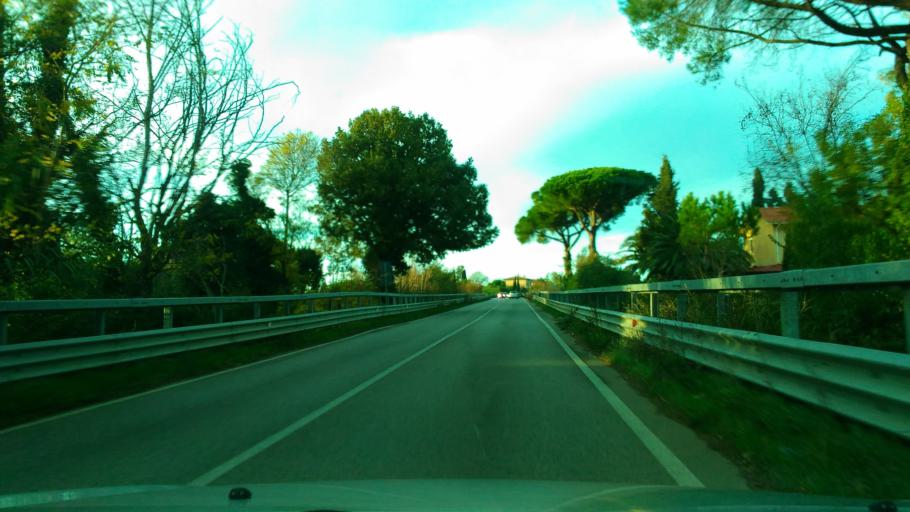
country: IT
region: Tuscany
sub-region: Provincia di Livorno
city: S.P. in Palazzi
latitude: 43.3629
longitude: 10.5095
